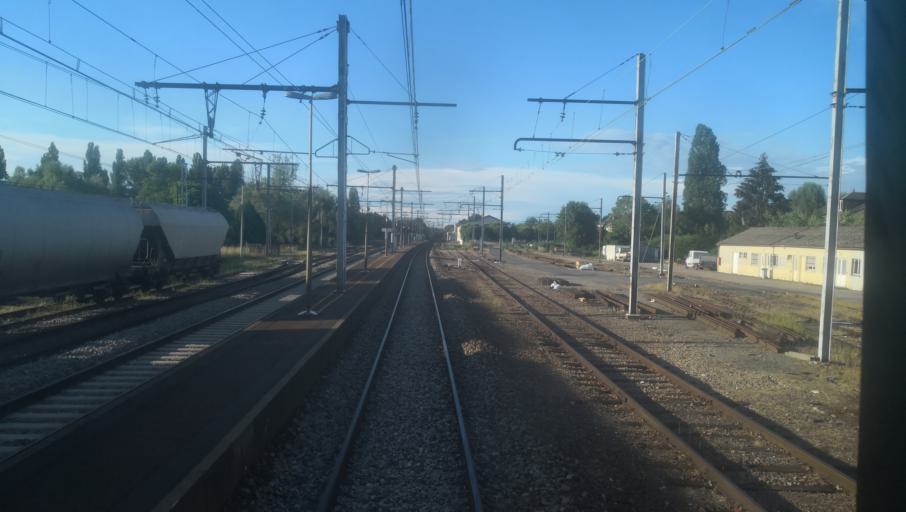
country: FR
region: Centre
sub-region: Departement de l'Indre
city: Issoudun
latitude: 46.9459
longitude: 1.9840
